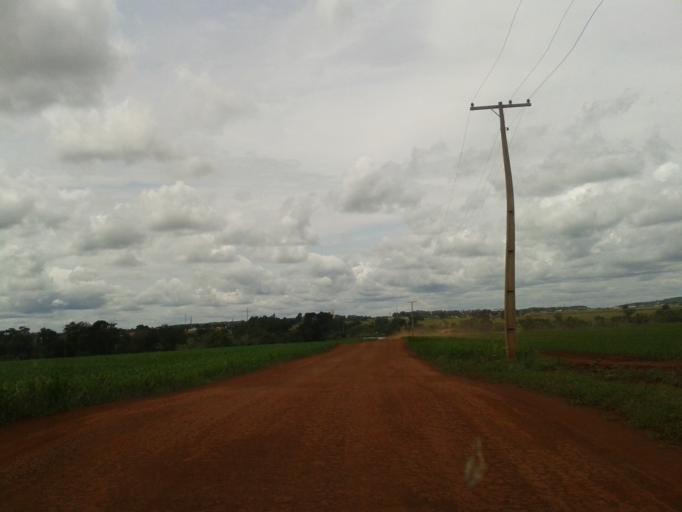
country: BR
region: Minas Gerais
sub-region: Centralina
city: Centralina
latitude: -18.5927
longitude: -49.2180
